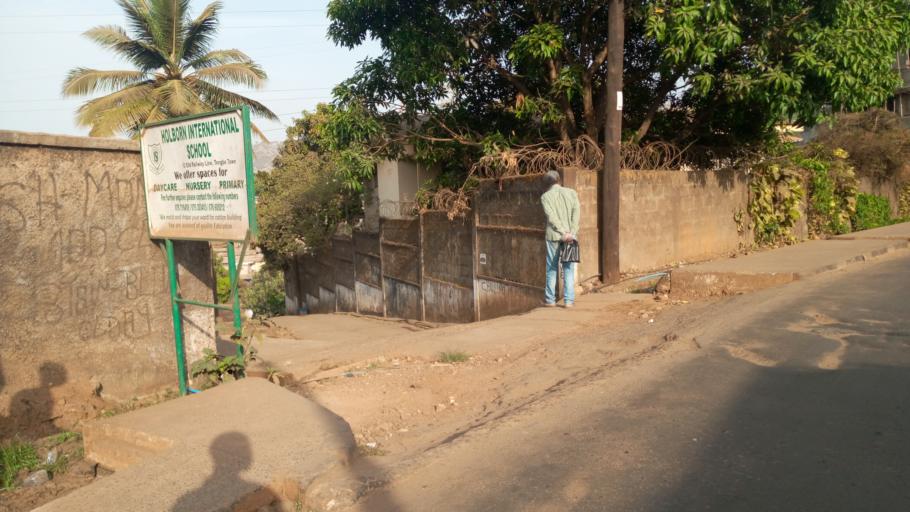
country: SL
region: Western Area
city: Freetown
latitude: 8.4737
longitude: -13.2520
